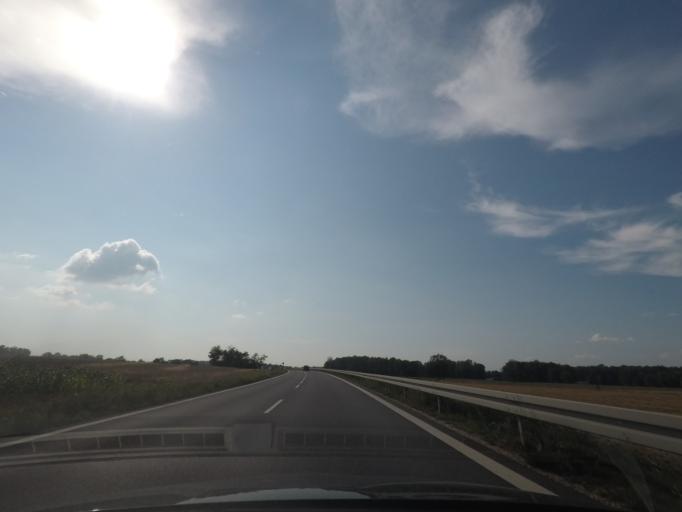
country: PL
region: Silesian Voivodeship
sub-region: Powiat pszczynski
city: Piasek
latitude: 50.0012
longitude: 18.9320
